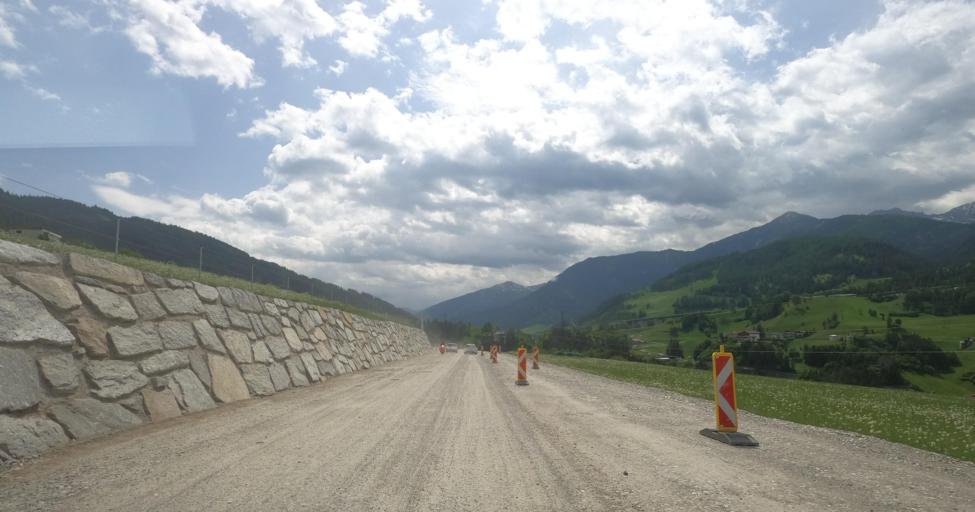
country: AT
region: Tyrol
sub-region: Politischer Bezirk Innsbruck Land
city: Pfons
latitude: 47.1469
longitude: 11.4569
